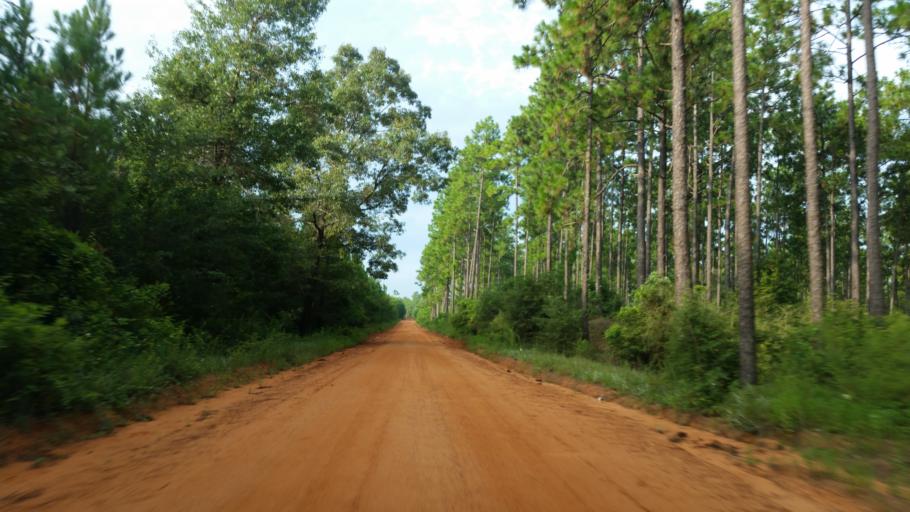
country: US
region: Alabama
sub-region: Escambia County
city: Atmore
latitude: 30.9139
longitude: -87.5800
